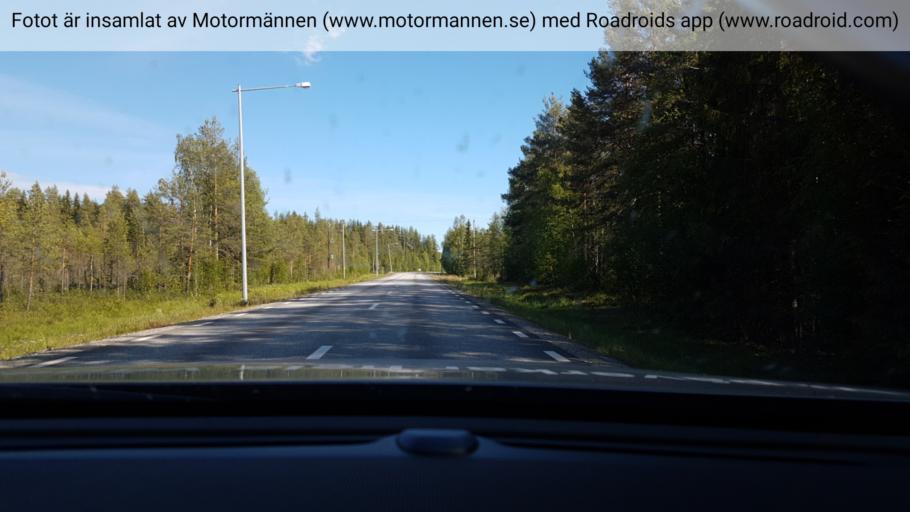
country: SE
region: Vaesterbotten
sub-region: Lycksele Kommun
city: Lycksele
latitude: 64.6923
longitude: 18.3991
